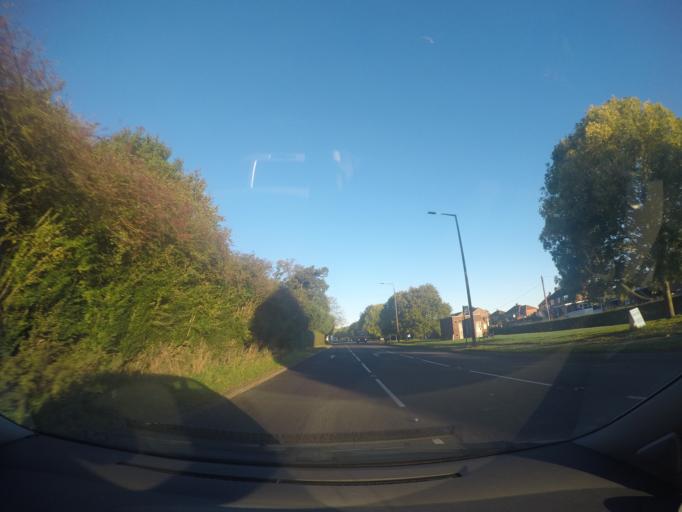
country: GB
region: England
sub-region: City of York
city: Skelton
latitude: 53.9826
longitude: -1.1178
